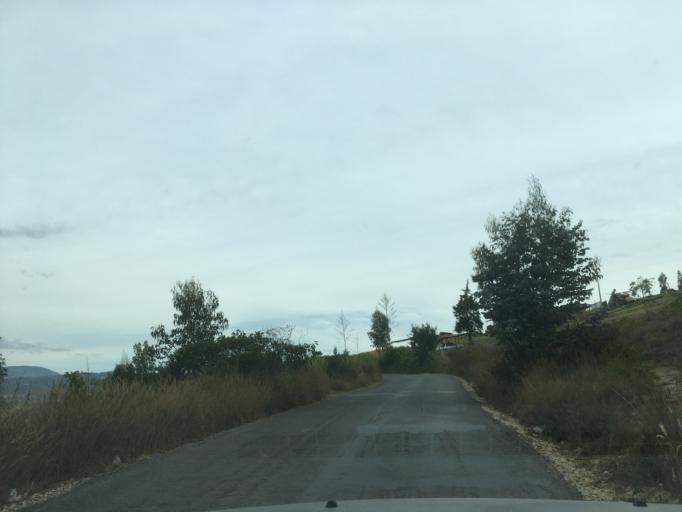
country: CO
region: Boyaca
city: Firavitoba
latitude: 5.6762
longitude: -73.0130
